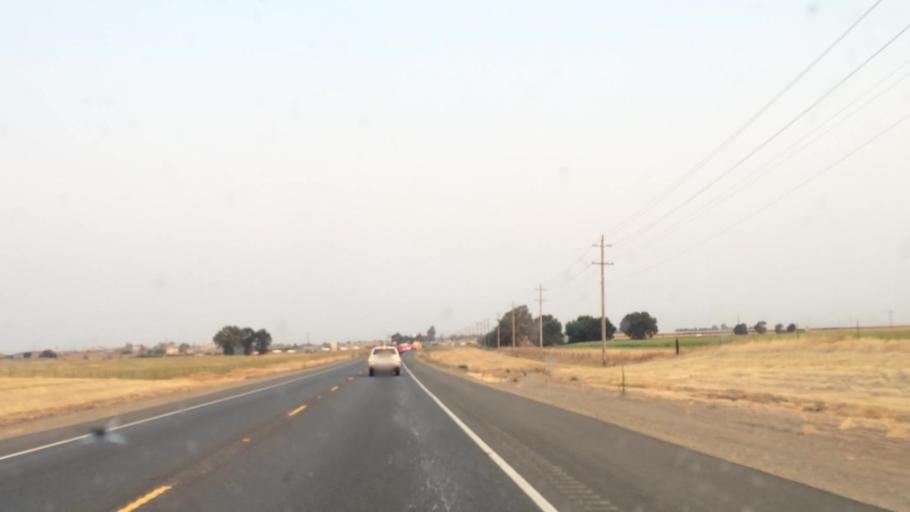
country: US
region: California
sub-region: Sacramento County
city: Wilton
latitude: 38.5051
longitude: -121.2369
